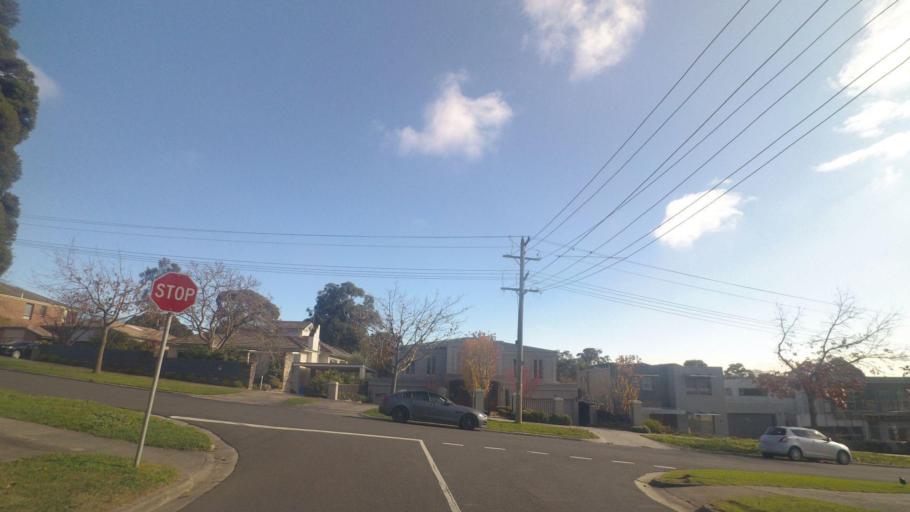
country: AU
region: Victoria
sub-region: Whitehorse
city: Mont Albert North
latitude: -37.8003
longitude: 145.1003
